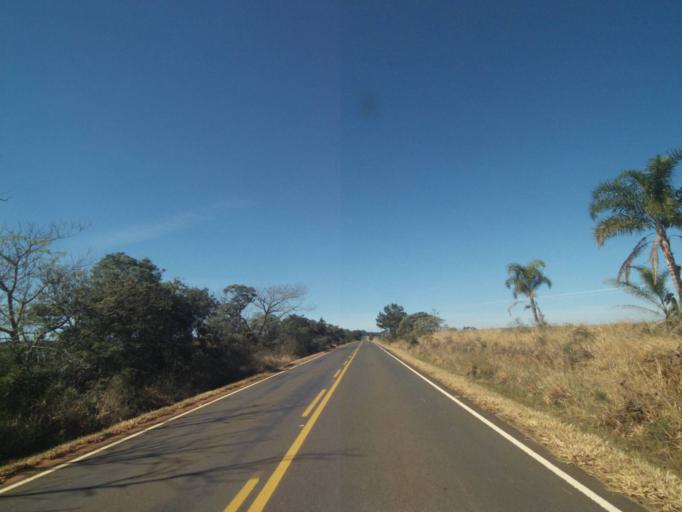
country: BR
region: Parana
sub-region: Tibagi
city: Tibagi
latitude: -24.4871
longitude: -50.4711
